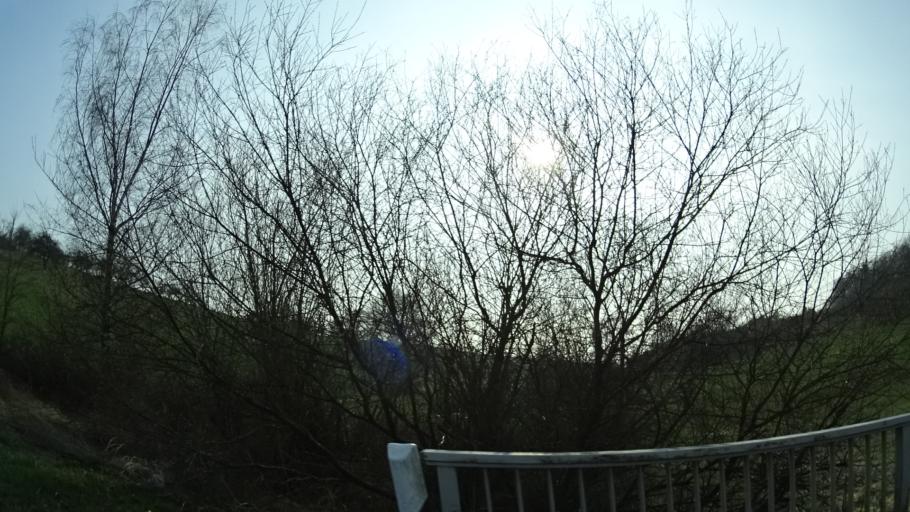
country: DE
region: Rheinland-Pfalz
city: Oberstaufenbach
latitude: 49.5057
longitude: 7.5227
